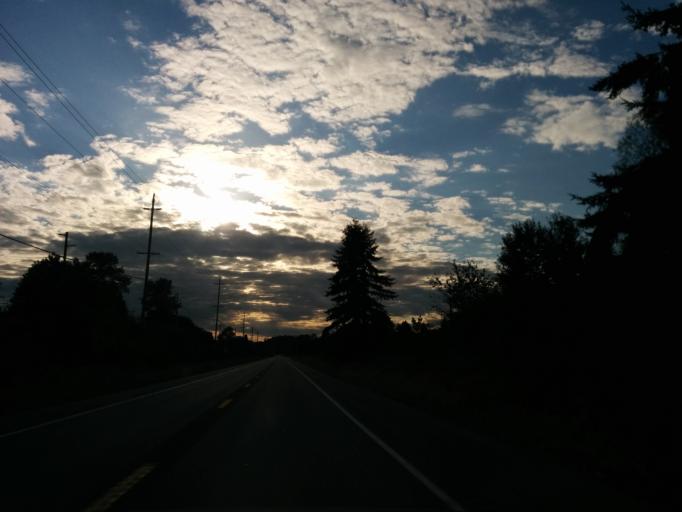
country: US
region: Washington
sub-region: Snohomish County
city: Woods Creek
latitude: 47.8556
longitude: -121.9212
